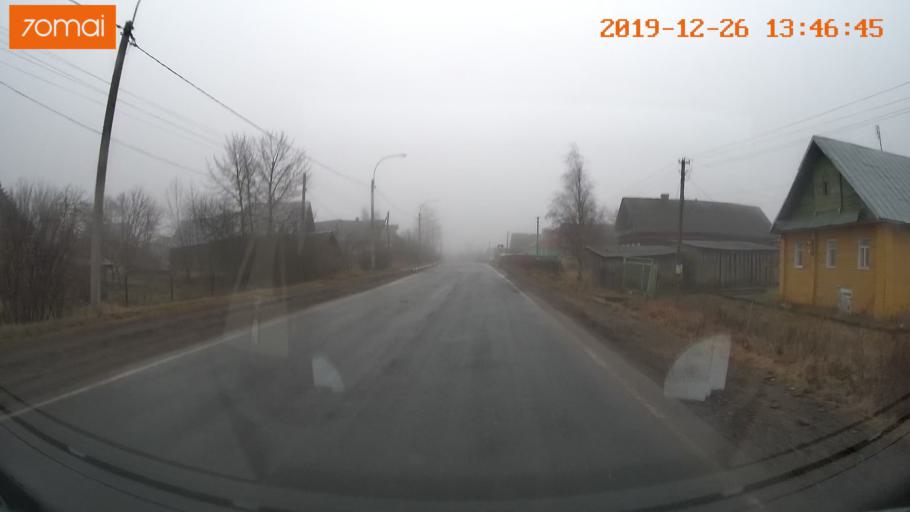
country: RU
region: Vologda
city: Sheksna
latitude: 58.6893
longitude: 38.5290
